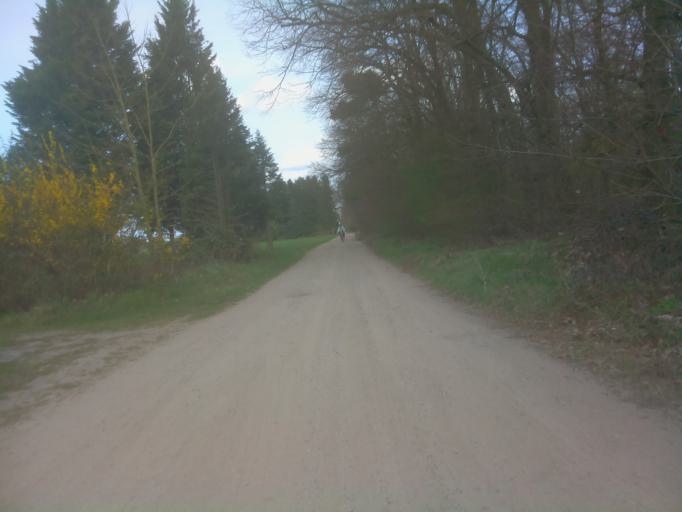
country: DE
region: Hesse
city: Lampertheim
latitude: 49.5736
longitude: 8.4955
